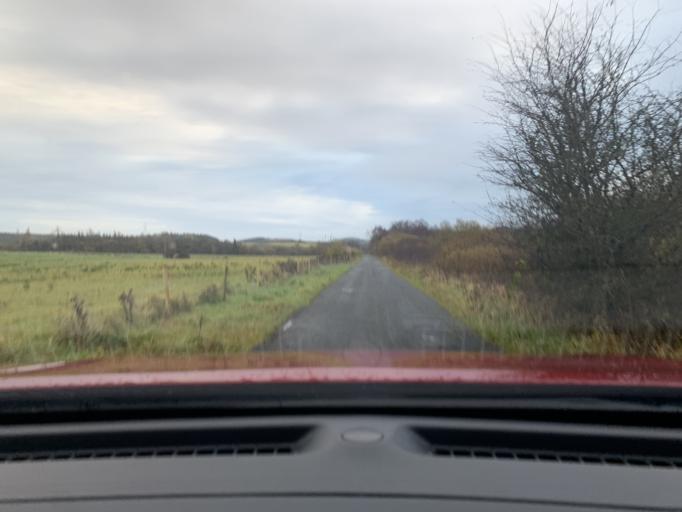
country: IE
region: Connaught
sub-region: Sligo
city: Ballymote
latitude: 54.0154
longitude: -8.5044
